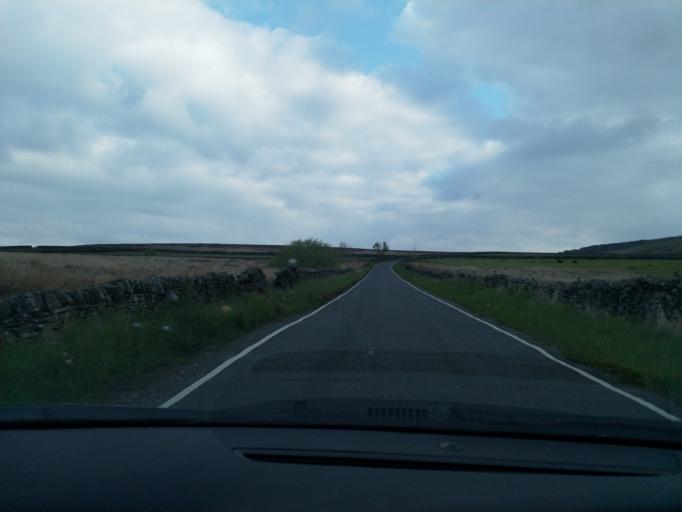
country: GB
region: England
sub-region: Derbyshire
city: Hathersage
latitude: 53.3362
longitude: -1.6325
